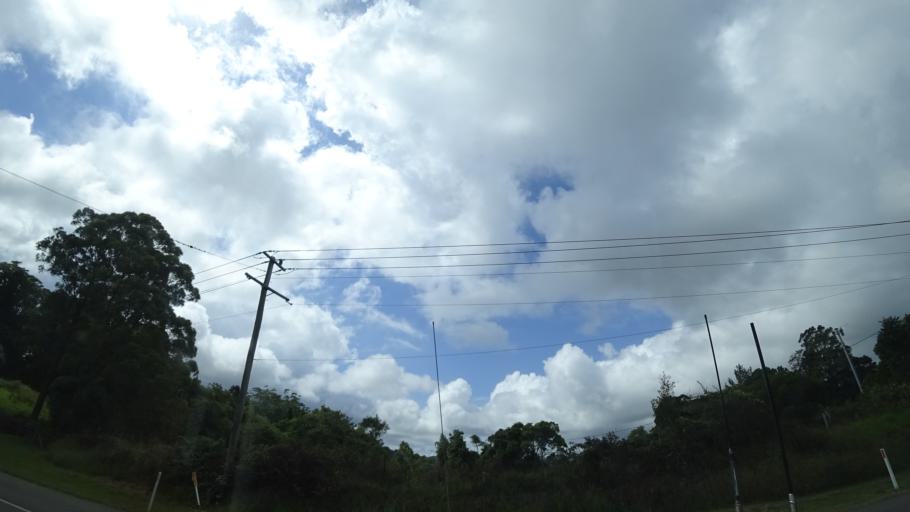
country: AU
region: Queensland
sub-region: Moreton Bay
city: Highvale
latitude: -27.3345
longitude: 152.7658
